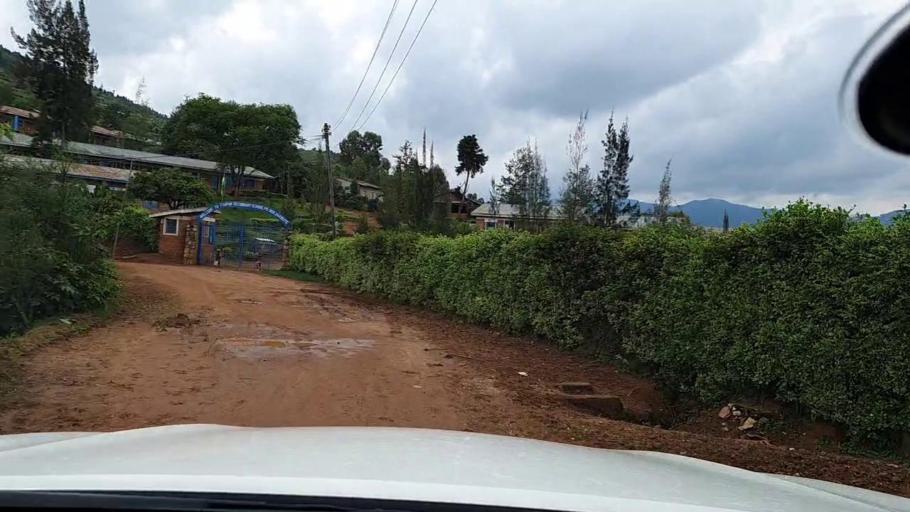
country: RW
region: Western Province
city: Kibuye
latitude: -2.1882
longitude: 29.2965
